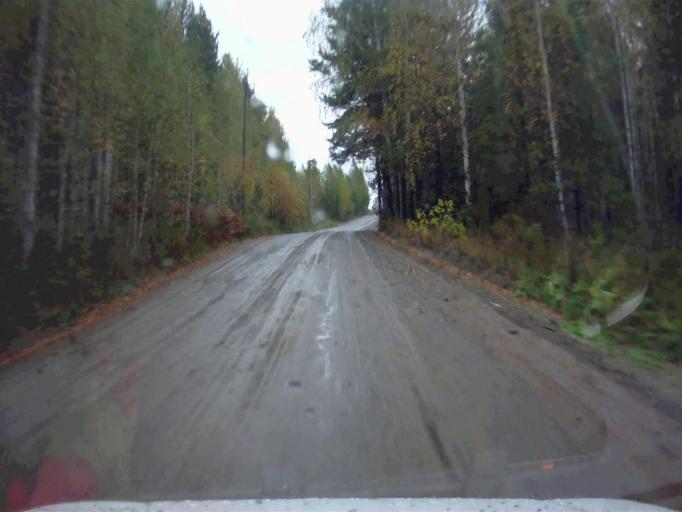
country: RU
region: Chelyabinsk
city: Kyshtym
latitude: 55.7521
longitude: 60.4868
